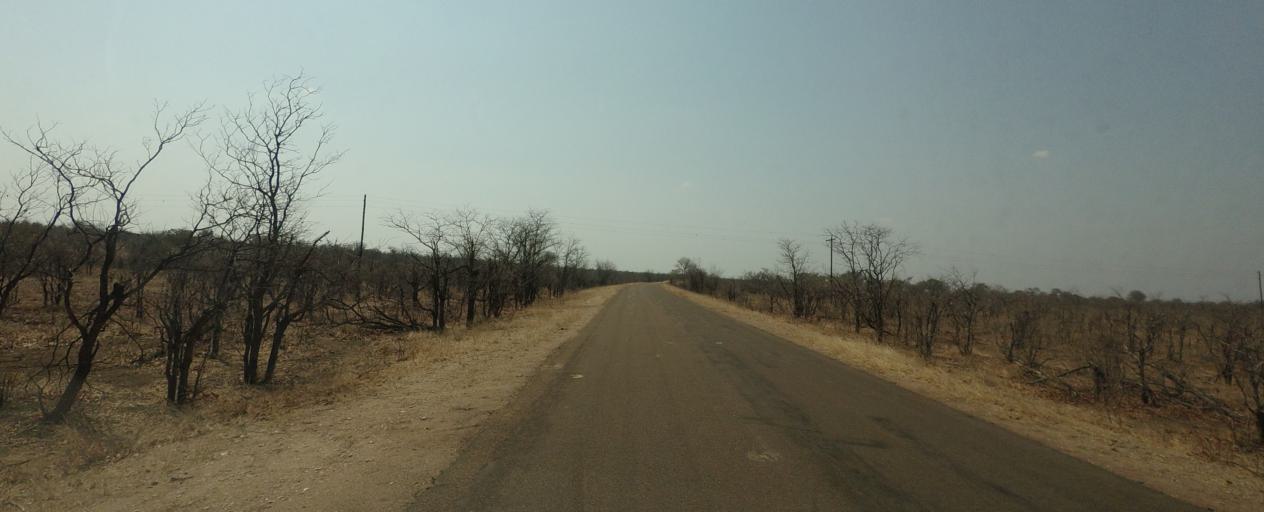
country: ZA
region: Limpopo
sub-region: Mopani District Municipality
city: Giyani
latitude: -23.2401
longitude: 31.3146
